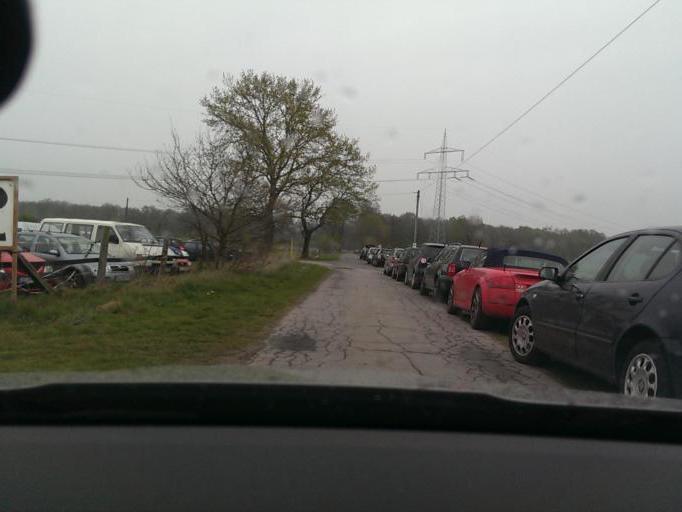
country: DE
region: Lower Saxony
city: Steimbke
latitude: 52.6023
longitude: 9.4541
